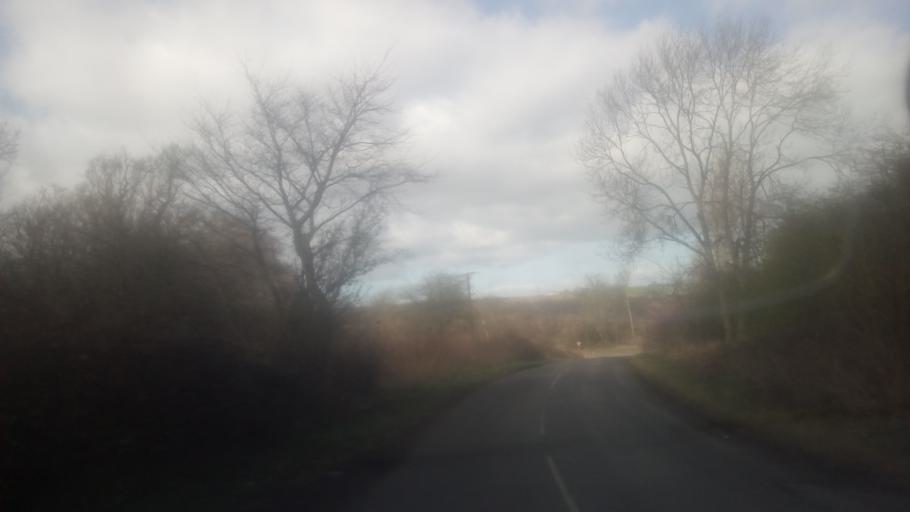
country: GB
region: Scotland
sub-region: East Lothian
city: Ormiston
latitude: 55.8946
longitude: -2.9601
